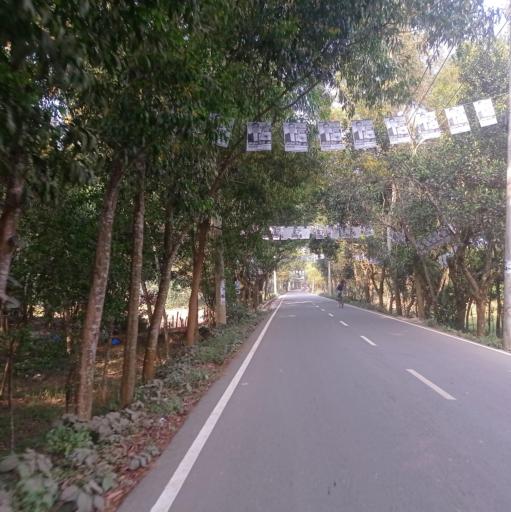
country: BD
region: Dhaka
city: Bhairab Bazar
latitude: 24.0408
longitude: 90.8331
